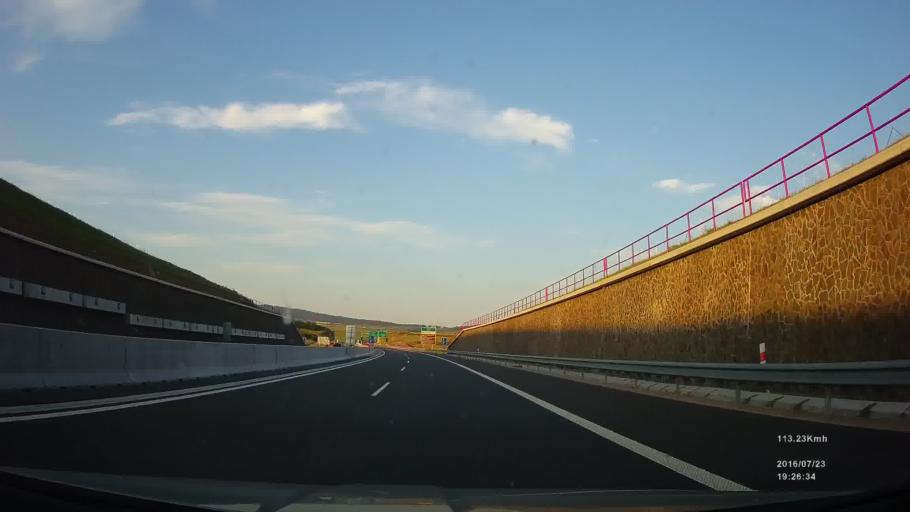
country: SK
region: Presovsky
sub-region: Okres Presov
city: Levoca
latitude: 49.0005
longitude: 20.5604
